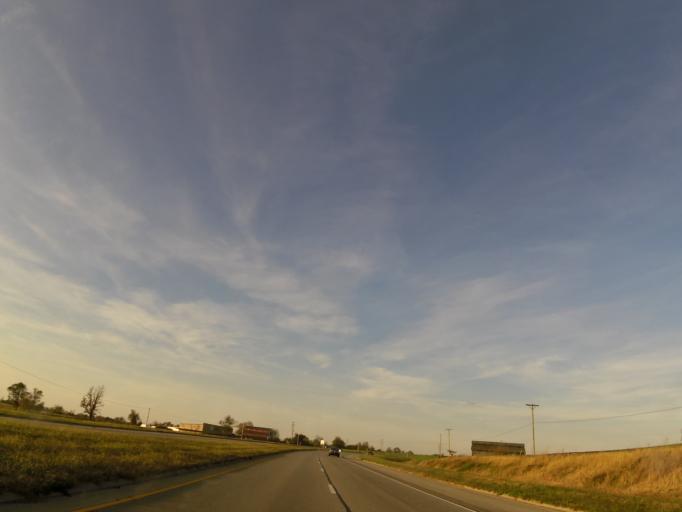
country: US
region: Kentucky
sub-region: Garrard County
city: Lancaster
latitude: 37.6964
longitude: -84.6660
